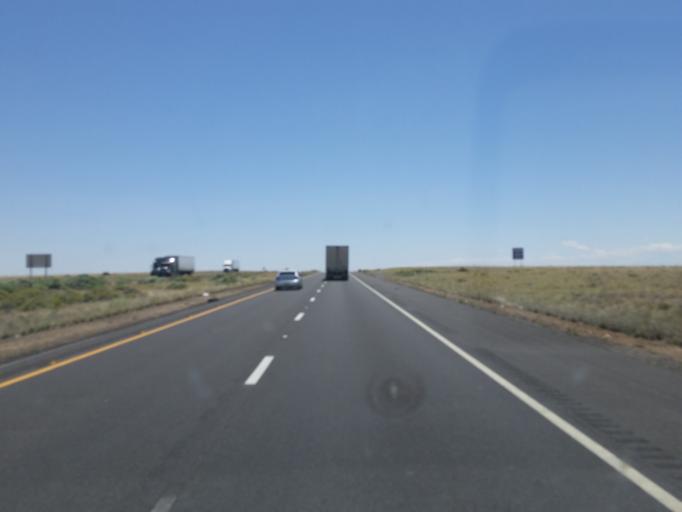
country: US
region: Arizona
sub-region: Coconino County
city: Flagstaff
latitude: 35.1352
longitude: -111.2009
